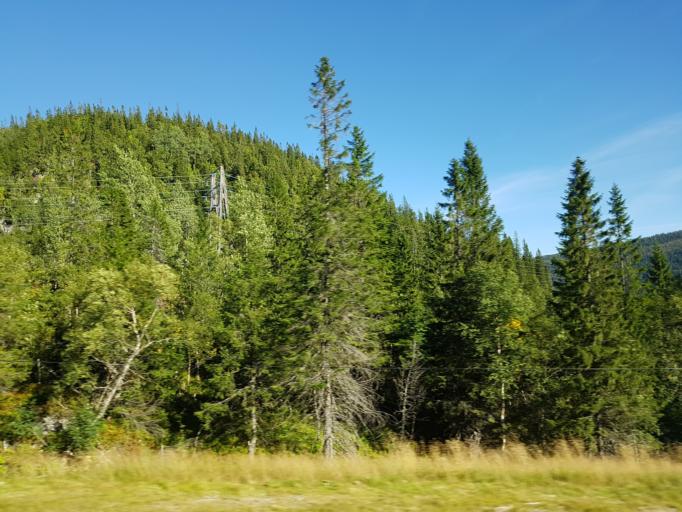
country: NO
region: Sor-Trondelag
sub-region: Afjord
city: A i Afjord
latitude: 63.6942
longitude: 10.2436
